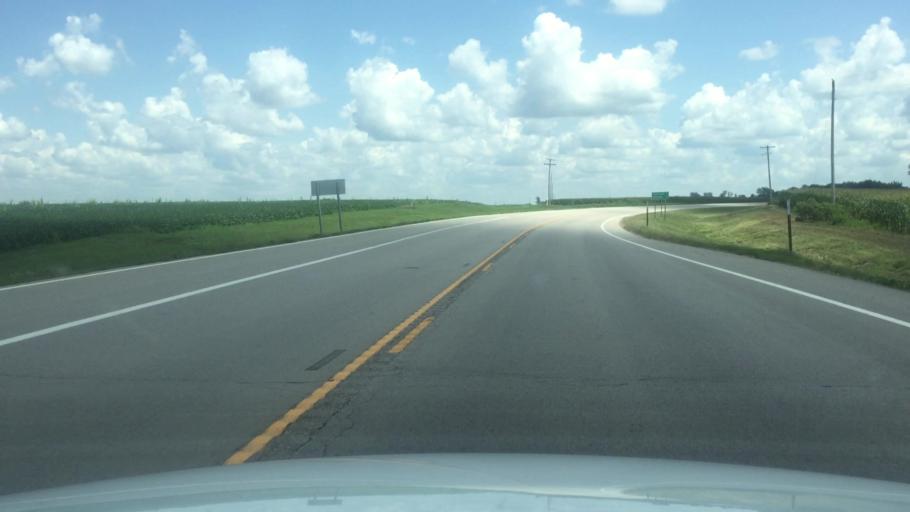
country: US
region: Kansas
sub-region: Brown County
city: Horton
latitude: 39.6674
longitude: -95.4236
